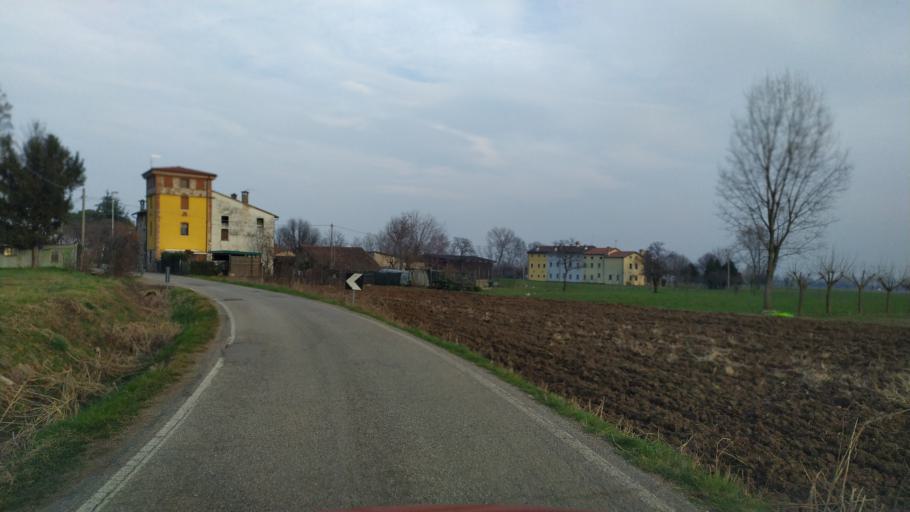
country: IT
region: Veneto
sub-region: Provincia di Vicenza
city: Marano Vicentino
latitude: 45.6794
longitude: 11.4433
